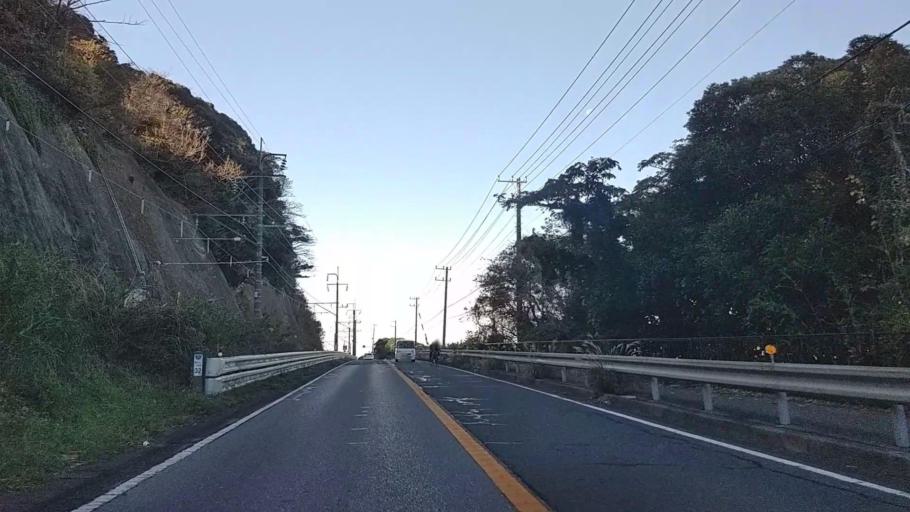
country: JP
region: Chiba
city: Futtsu
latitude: 35.2134
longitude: 139.8517
